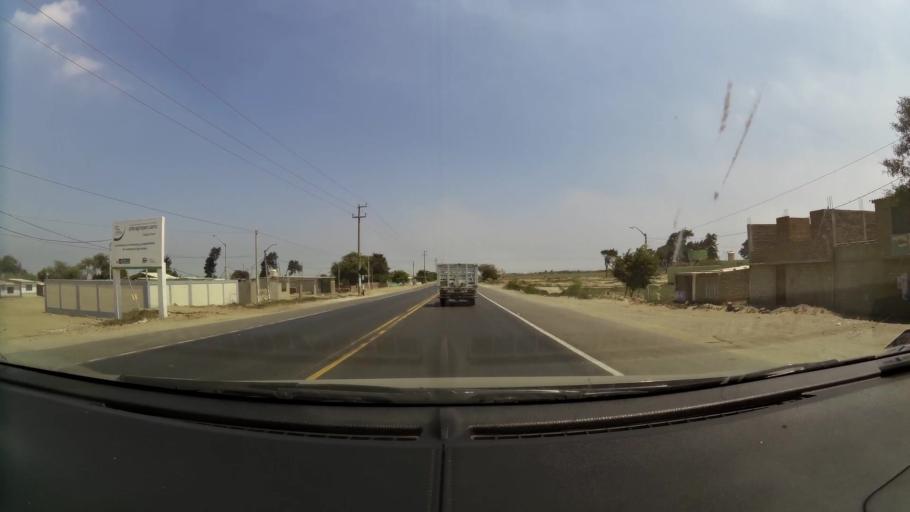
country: PE
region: La Libertad
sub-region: Provincia de Pacasmayo
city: San Pedro de Lloc
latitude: -7.4182
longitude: -79.5259
